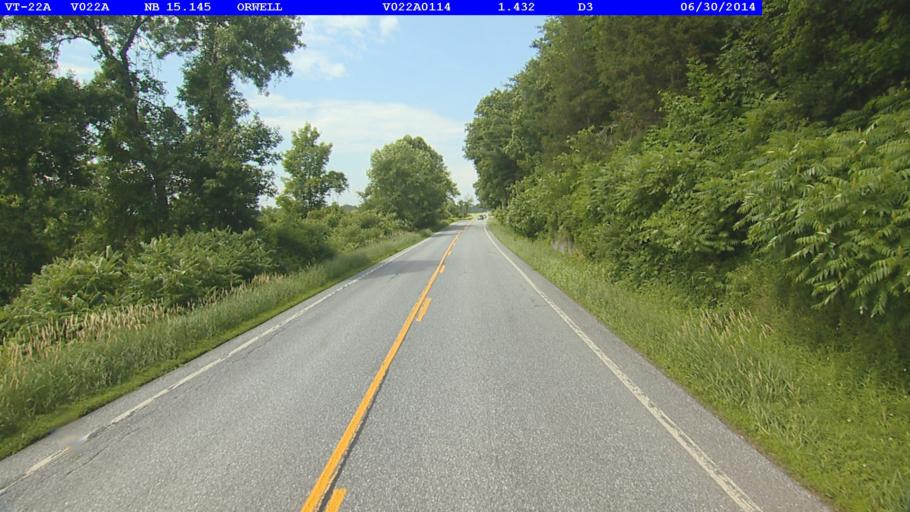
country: US
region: New York
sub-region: Essex County
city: Ticonderoga
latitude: 43.7777
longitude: -73.3079
